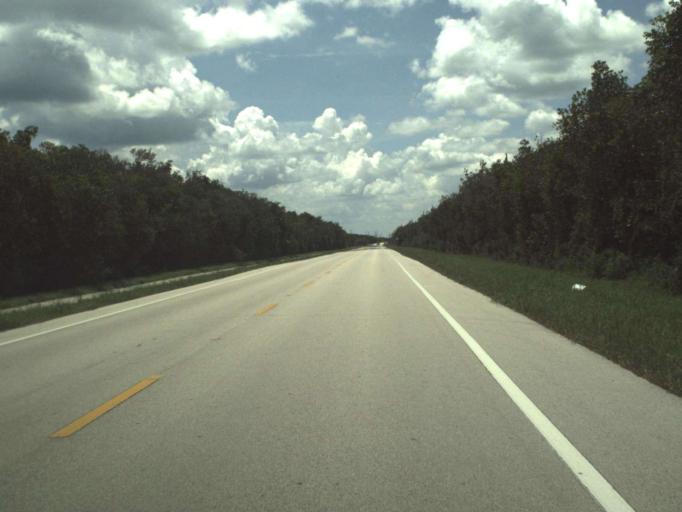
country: US
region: Florida
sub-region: Saint Lucie County
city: Indian River Estates
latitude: 27.3734
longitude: -80.2534
